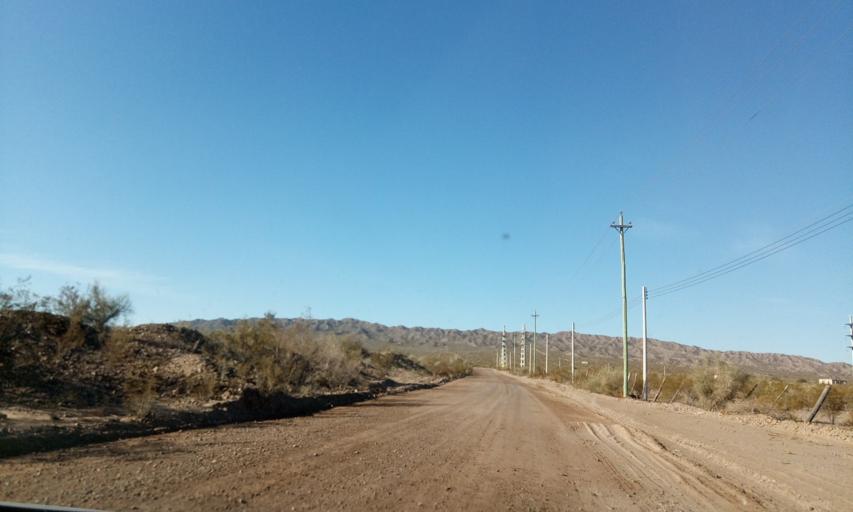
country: AR
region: San Juan
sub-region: Departamento de Rivadavia
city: Rivadavia
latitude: -31.4246
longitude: -68.6715
